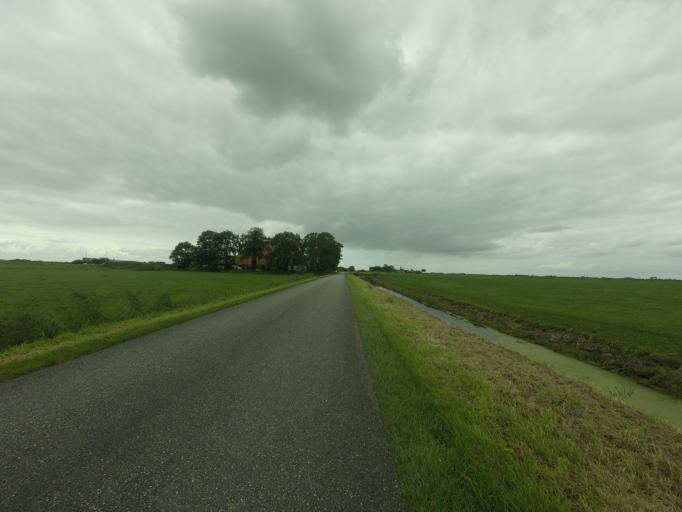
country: NL
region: Friesland
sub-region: Sudwest Fryslan
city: Bolsward
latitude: 52.9862
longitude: 5.5318
